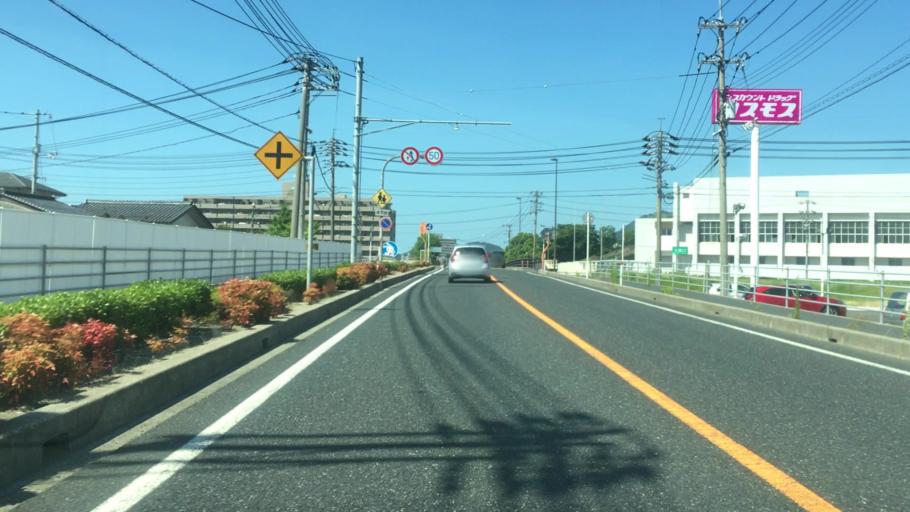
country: JP
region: Tottori
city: Tottori
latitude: 35.4829
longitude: 134.2198
